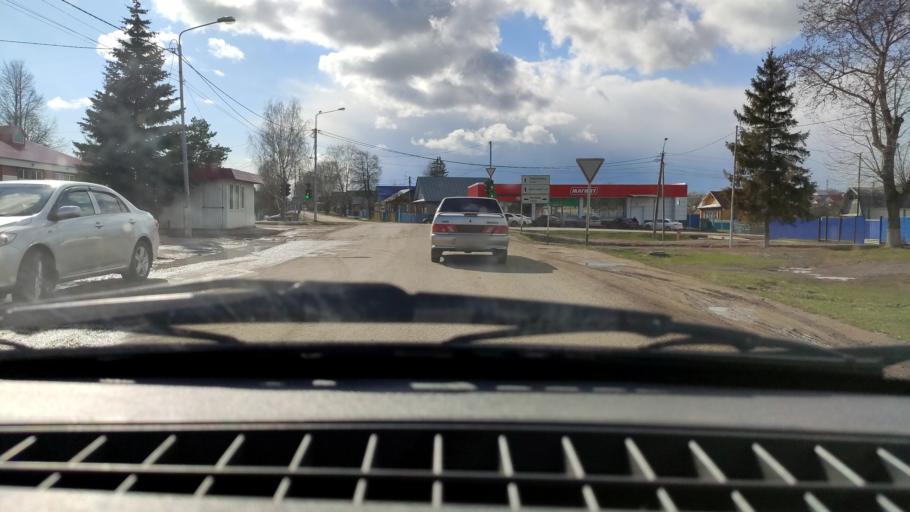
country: RU
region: Bashkortostan
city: Chekmagush
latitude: 55.1331
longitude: 54.6558
